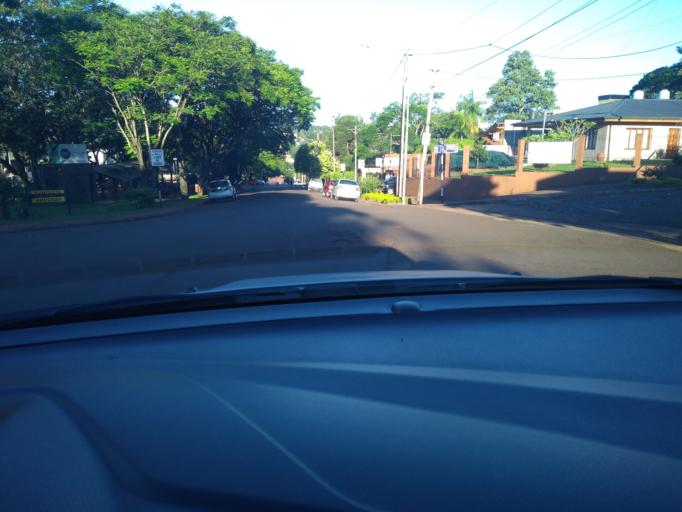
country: AR
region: Misiones
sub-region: Departamento de Obera
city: Obera
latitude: -27.4818
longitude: -55.1115
